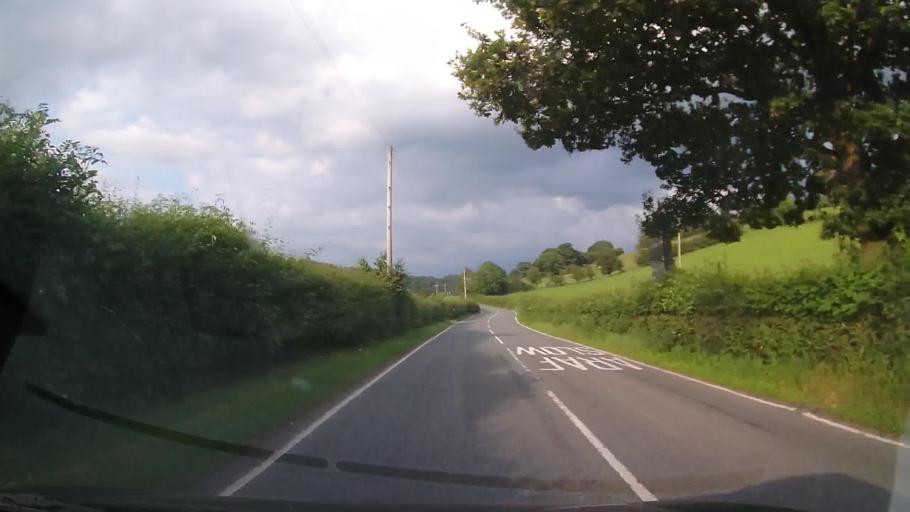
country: GB
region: Wales
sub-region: Gwynedd
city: Bala
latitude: 52.9083
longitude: -3.5491
